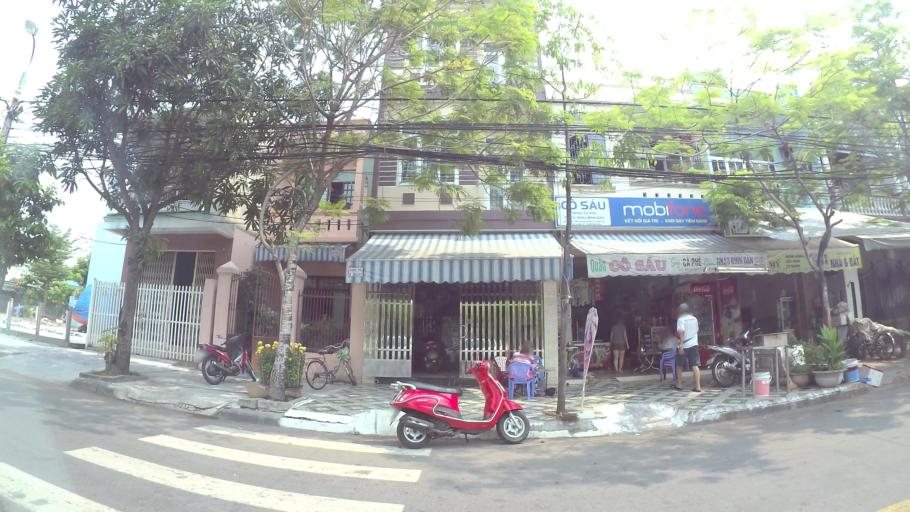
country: VN
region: Da Nang
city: Da Nang
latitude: 16.0888
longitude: 108.2349
